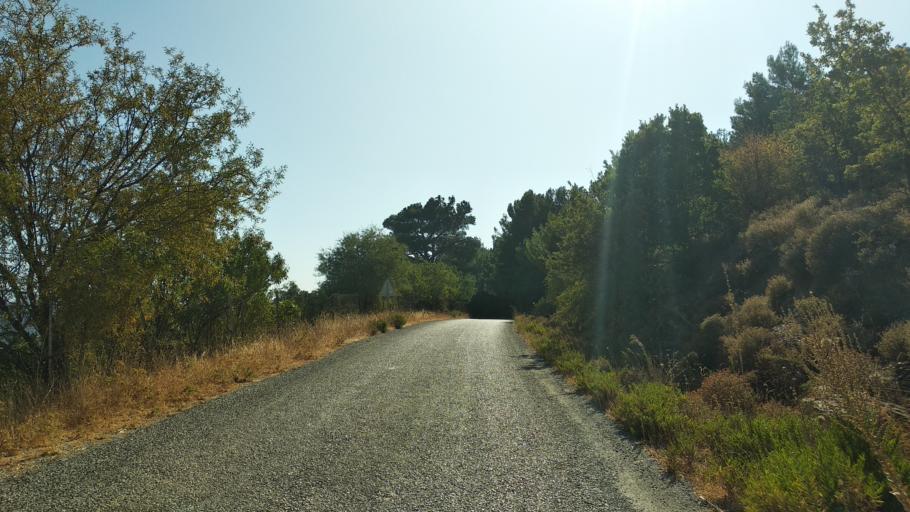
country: TR
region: Izmir
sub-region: Seferihisar
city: Seferhisar
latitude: 38.3243
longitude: 26.9398
